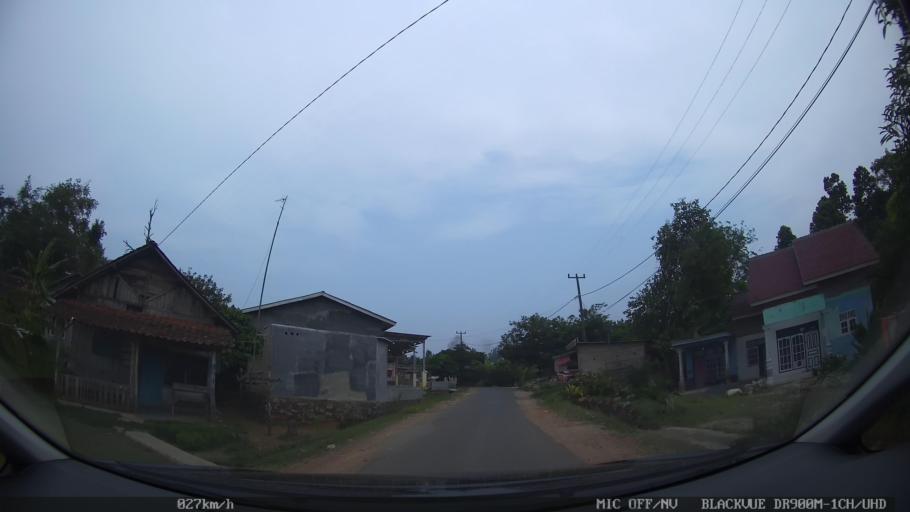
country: ID
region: Lampung
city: Panjang
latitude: -5.4222
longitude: 105.3533
